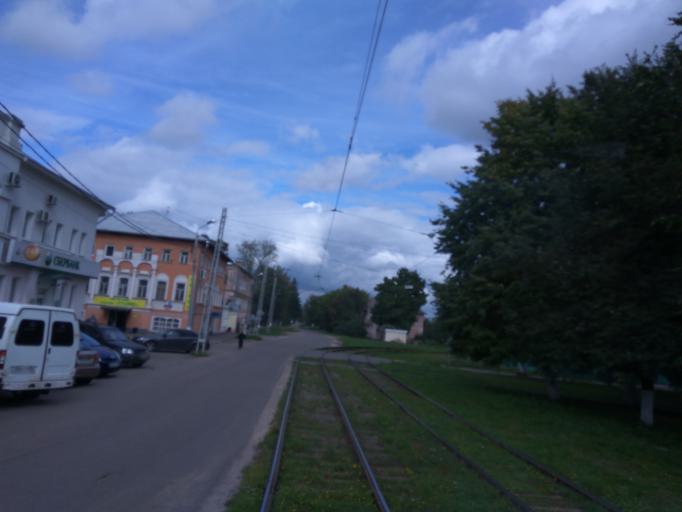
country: RU
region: Moskovskaya
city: Kolomna
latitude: 55.0989
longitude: 38.7757
